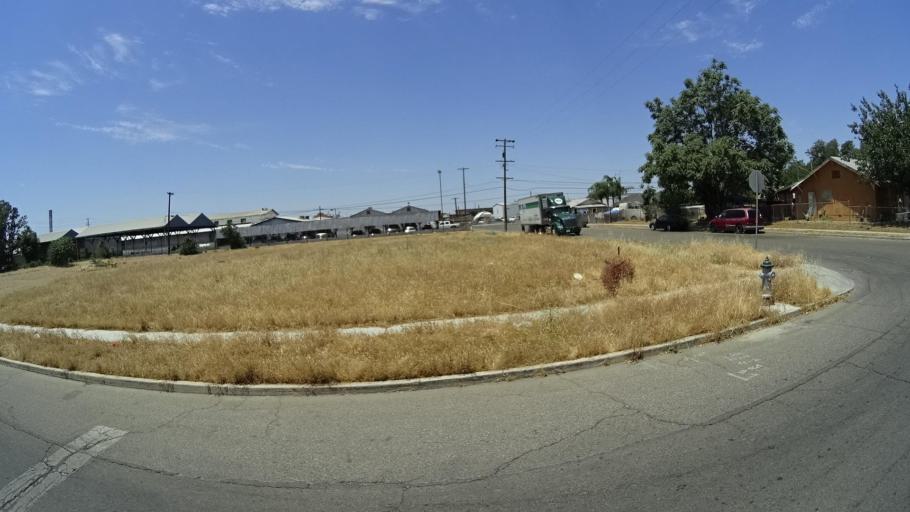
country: US
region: California
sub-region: Fresno County
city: Fresno
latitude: 36.7226
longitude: -119.7680
